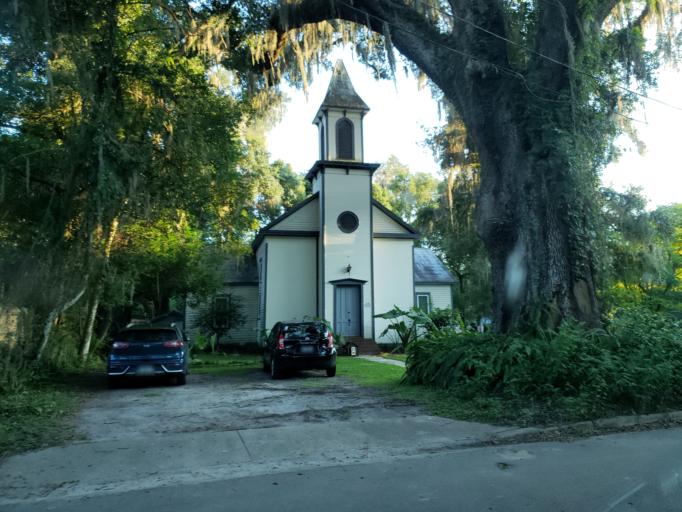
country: US
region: Florida
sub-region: Alachua County
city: Gainesville
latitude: 29.5032
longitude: -82.2823
